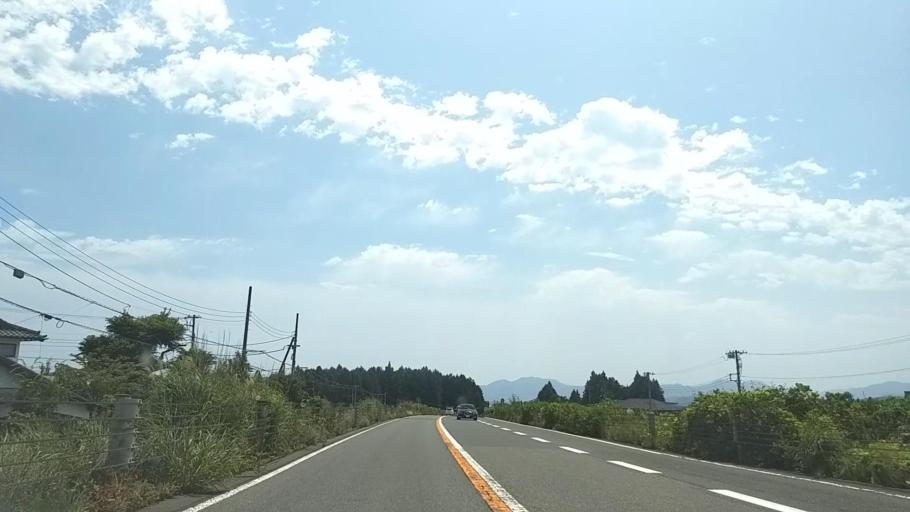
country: JP
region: Shizuoka
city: Fujinomiya
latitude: 35.2831
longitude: 138.6127
